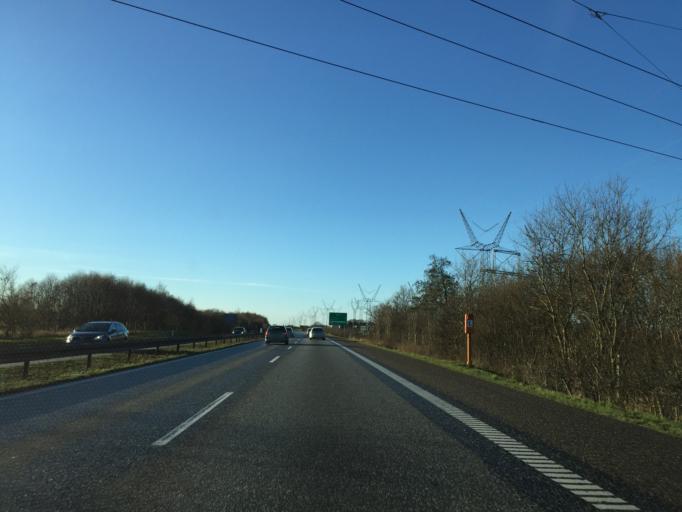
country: DK
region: South Denmark
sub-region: Odense Kommune
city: Neder Holluf
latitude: 55.3634
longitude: 10.5042
